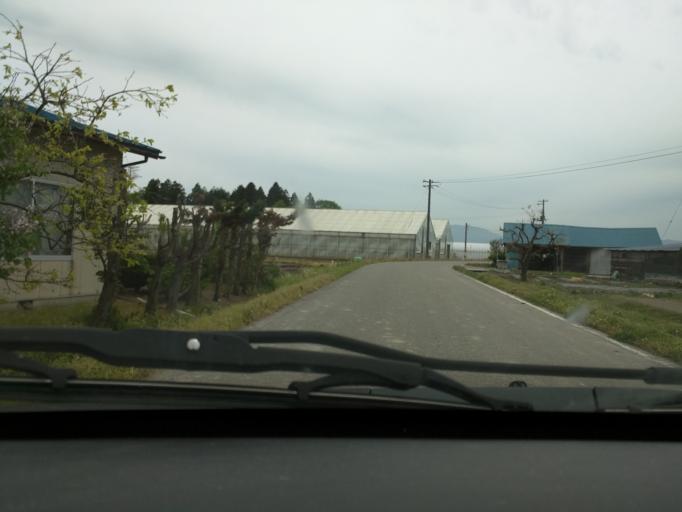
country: JP
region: Fukushima
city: Kitakata
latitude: 37.5384
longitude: 139.8632
